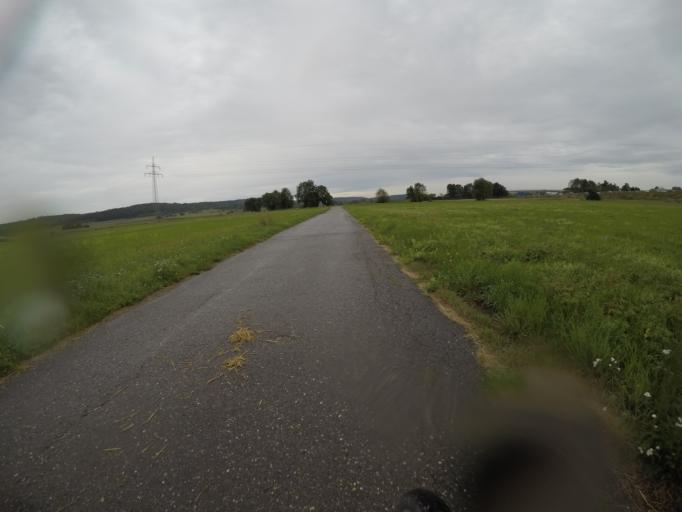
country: DE
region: Baden-Wuerttemberg
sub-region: Regierungsbezirk Stuttgart
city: Ehningen
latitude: 48.6413
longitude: 8.9343
